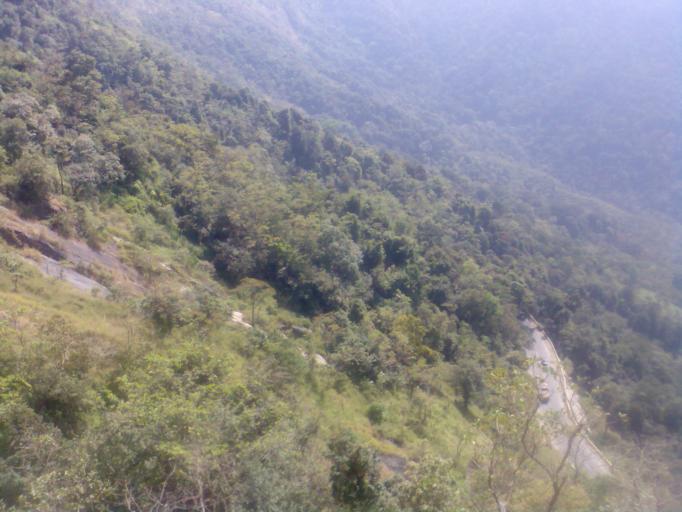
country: IN
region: Kerala
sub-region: Wayanad
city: Kalpetta
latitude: 11.5138
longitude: 76.0215
